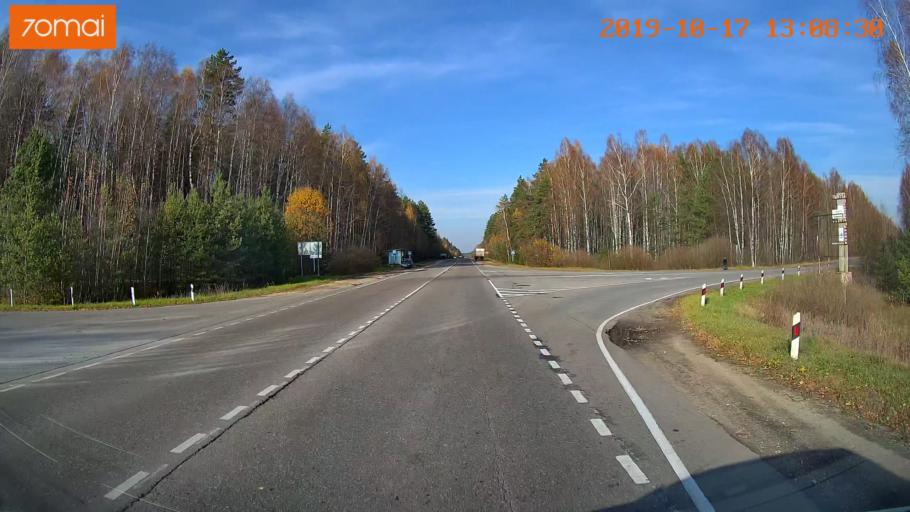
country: RU
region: Rjazan
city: Syntul
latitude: 54.9901
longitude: 41.2687
